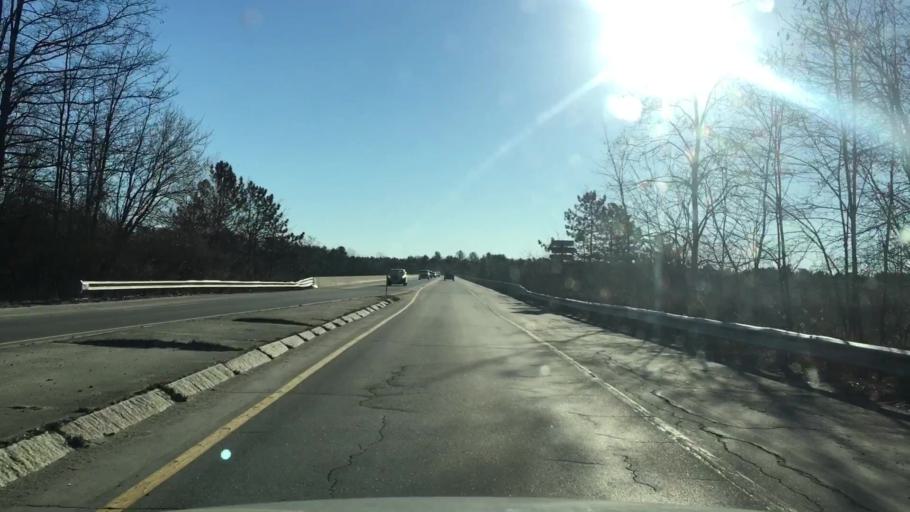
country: US
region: Maine
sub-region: Kennebec County
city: Waterville
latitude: 44.5325
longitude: -69.6490
